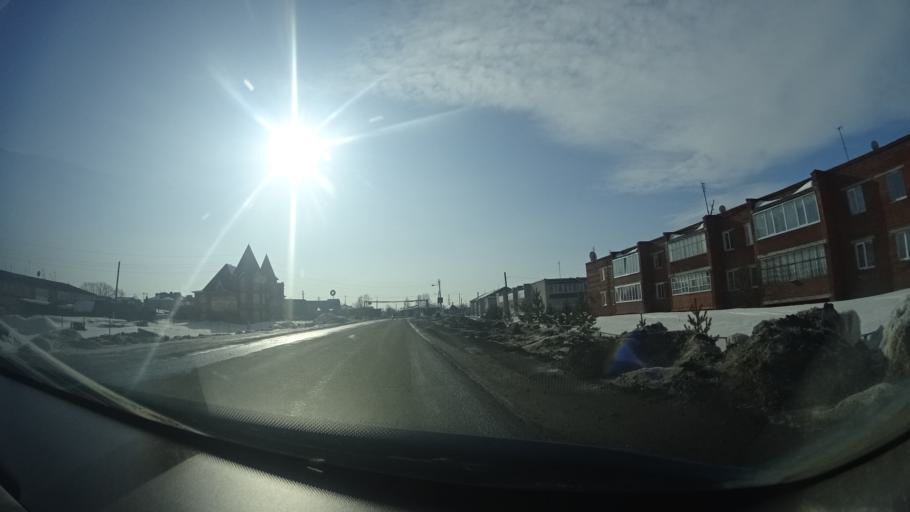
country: RU
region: Perm
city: Kuyeda
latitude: 56.4337
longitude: 55.5739
